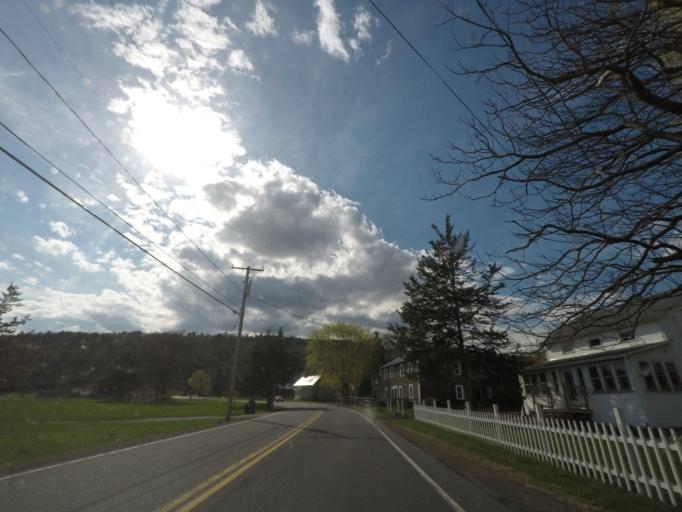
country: US
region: New York
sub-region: Albany County
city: Voorheesville
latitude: 42.5592
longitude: -73.9487
